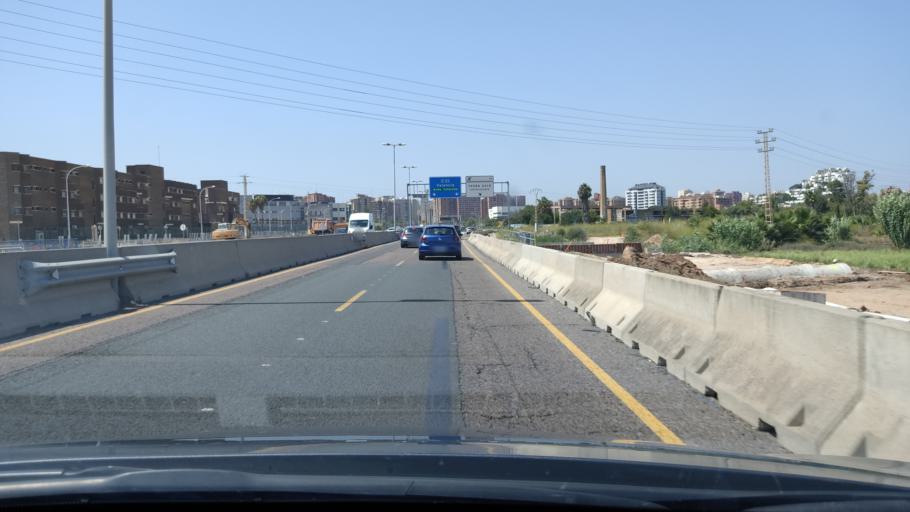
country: ES
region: Valencia
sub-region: Provincia de Valencia
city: Alboraya
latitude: 39.4856
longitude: -0.3457
